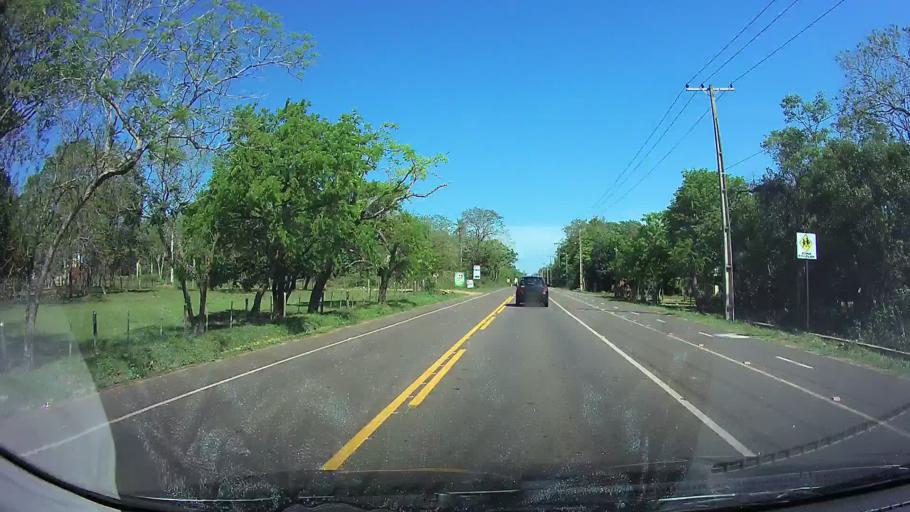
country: PY
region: Cordillera
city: San Bernardino
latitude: -25.2448
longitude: -57.3234
